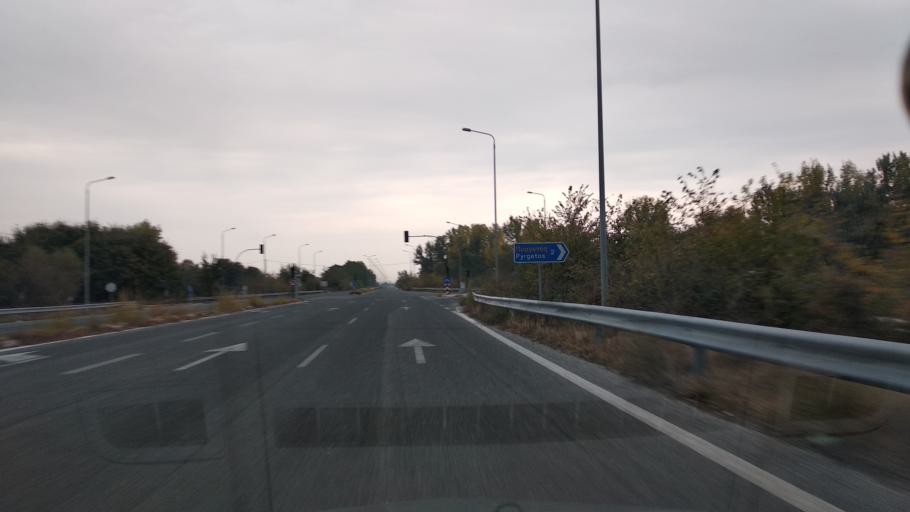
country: GR
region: Thessaly
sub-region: Trikala
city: Pyrgetos
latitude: 39.5402
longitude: 21.7359
